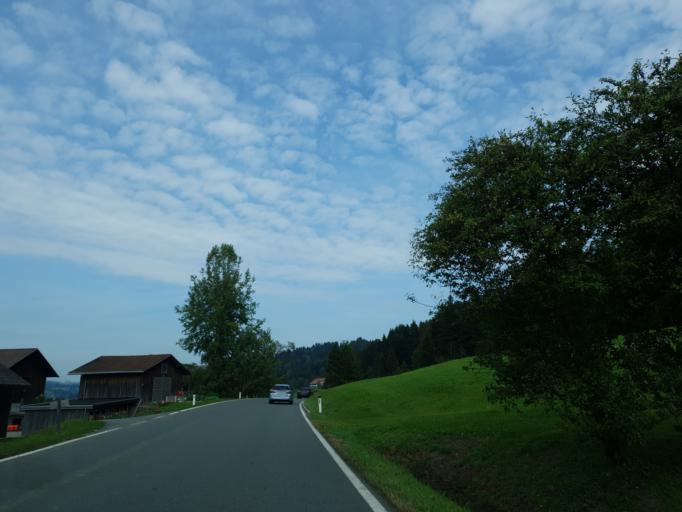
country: AT
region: Vorarlberg
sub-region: Politischer Bezirk Bregenz
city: Doren
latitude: 47.5034
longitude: 9.8628
